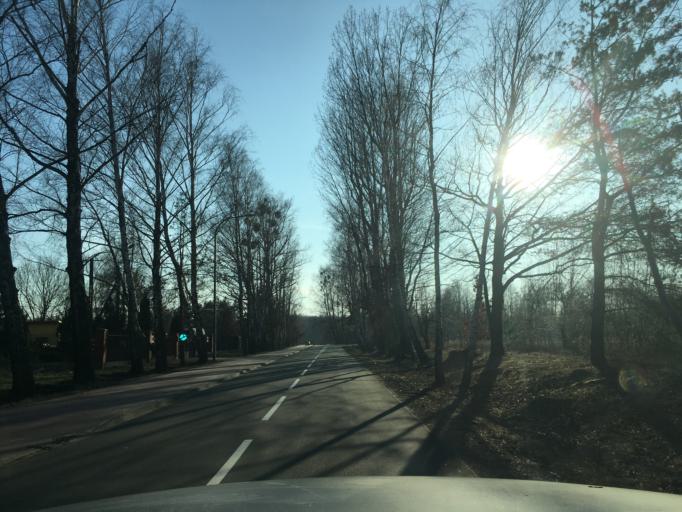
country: PL
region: Masovian Voivodeship
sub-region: Powiat pruszkowski
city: Nadarzyn
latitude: 52.0490
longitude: 20.7667
